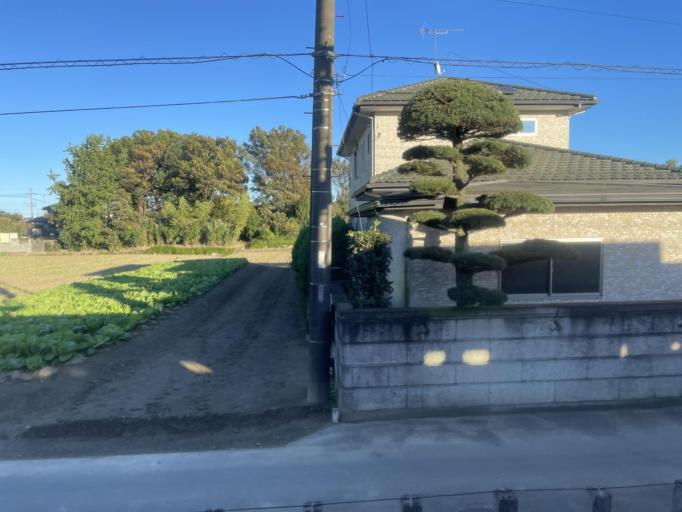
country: JP
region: Saitama
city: Satte
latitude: 36.1008
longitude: 139.7205
